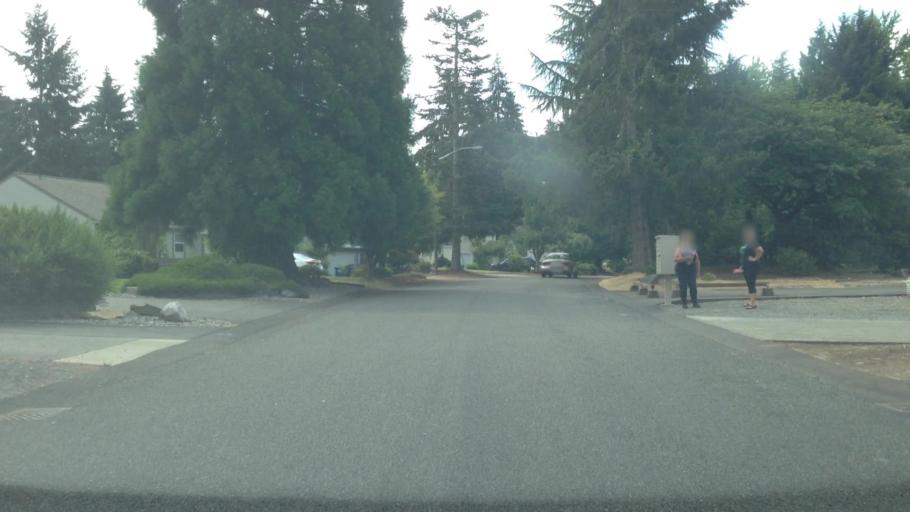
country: US
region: Washington
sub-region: Pierce County
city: South Hill
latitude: 47.1128
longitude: -122.3024
